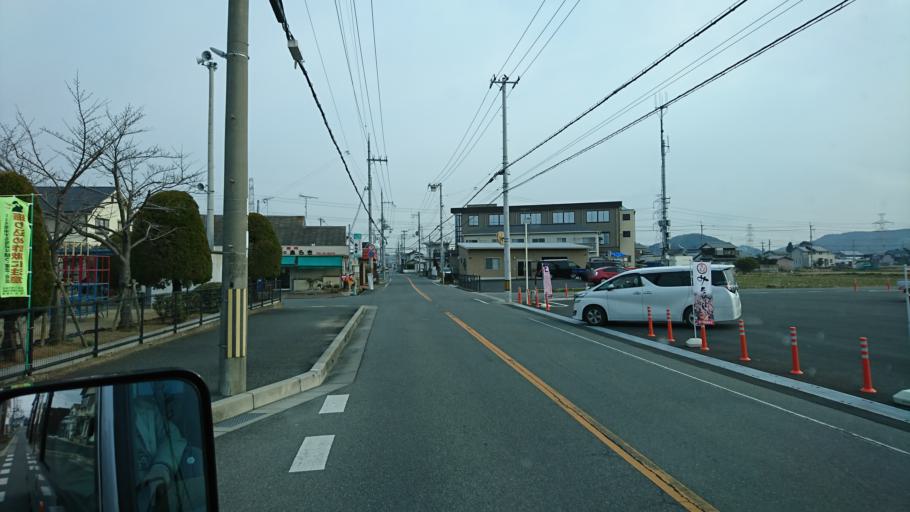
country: JP
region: Hyogo
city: Kakogawacho-honmachi
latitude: 34.7976
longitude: 134.8145
